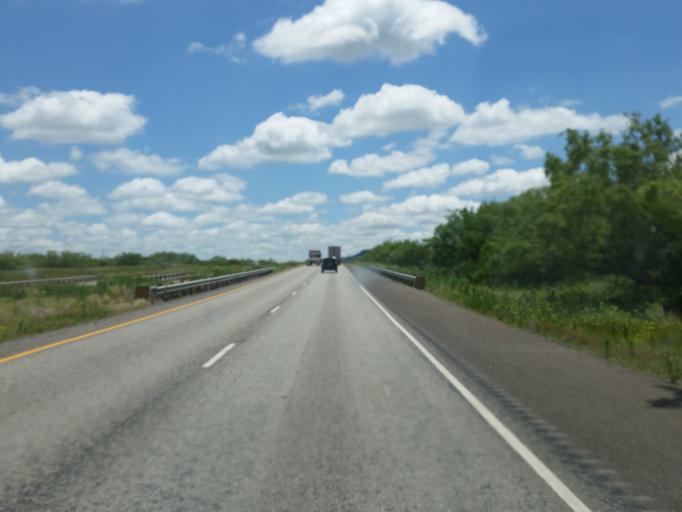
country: US
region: Texas
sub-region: Scurry County
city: Snyder
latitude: 32.9814
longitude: -101.1132
